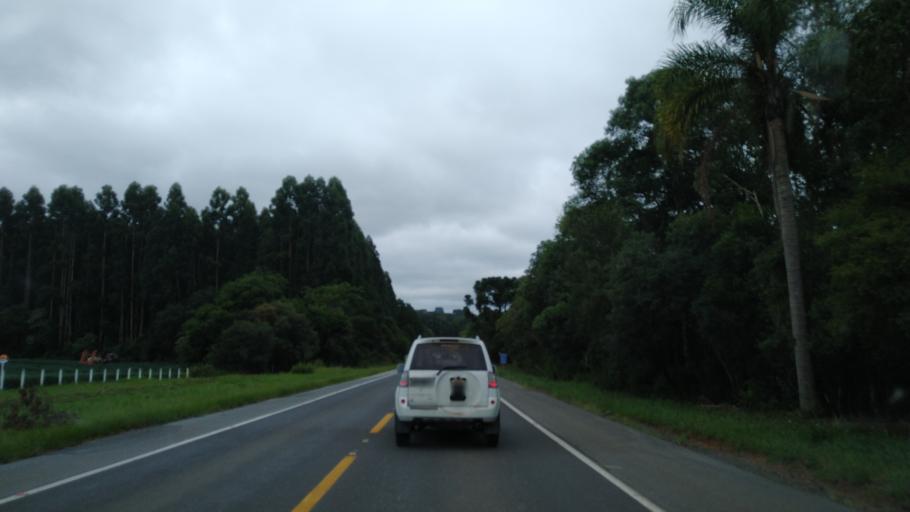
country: BR
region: Santa Catarina
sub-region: Tres Barras
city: Tres Barras
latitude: -26.1820
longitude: -50.2017
